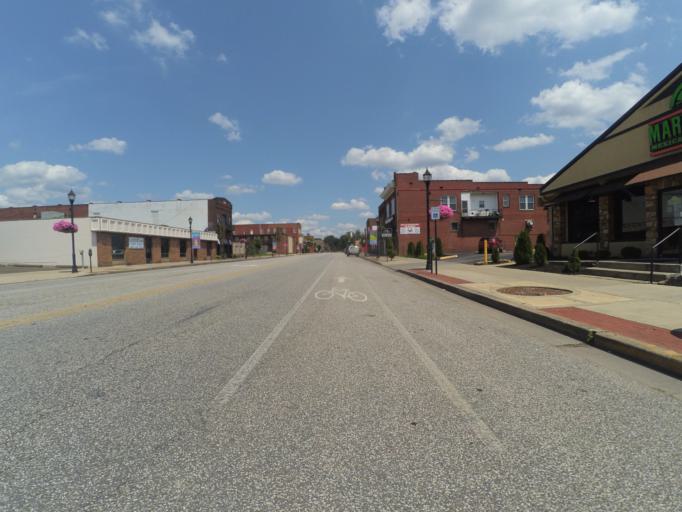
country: US
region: West Virginia
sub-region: Cabell County
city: Huntington
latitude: 38.4220
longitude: -82.4368
